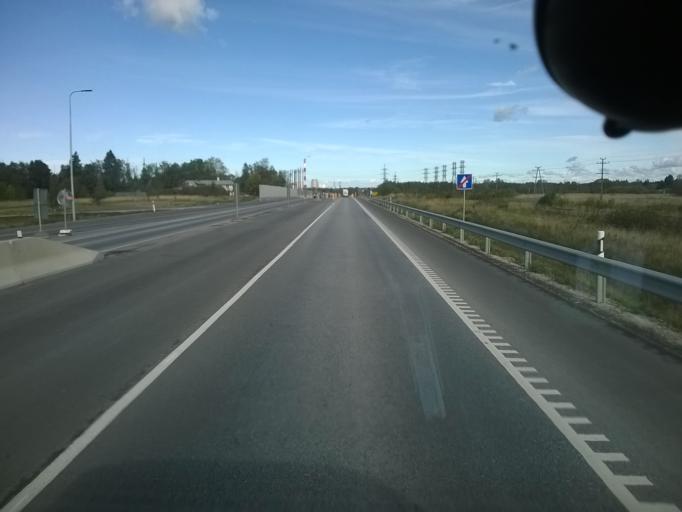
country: EE
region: Harju
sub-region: Joelaehtme vald
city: Loo
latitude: 59.4179
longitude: 24.9201
